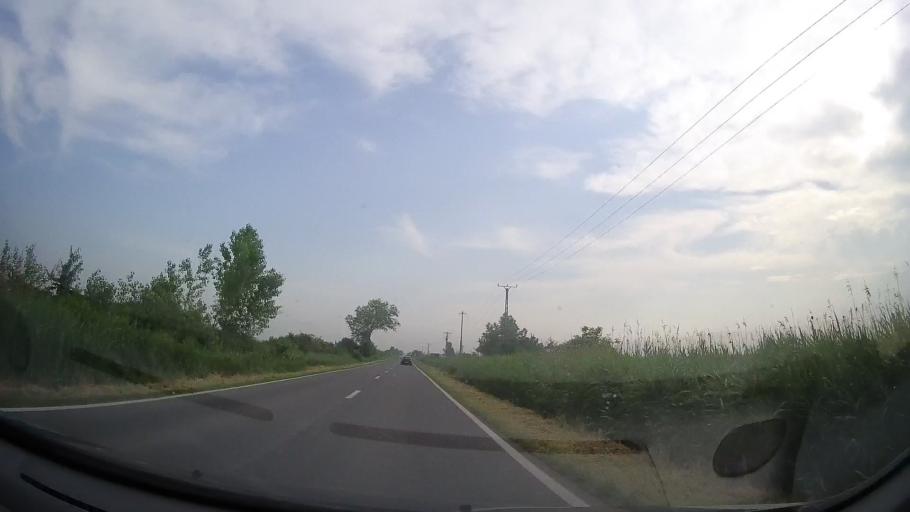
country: RO
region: Timis
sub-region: Comuna Sag
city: Sag
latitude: 45.6818
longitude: 21.1668
